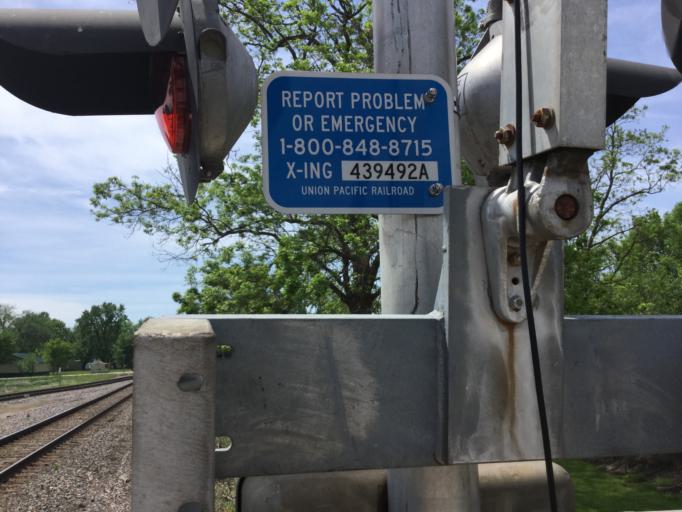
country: US
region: Kansas
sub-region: Coffey County
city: Burlington
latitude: 38.0801
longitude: -95.6310
